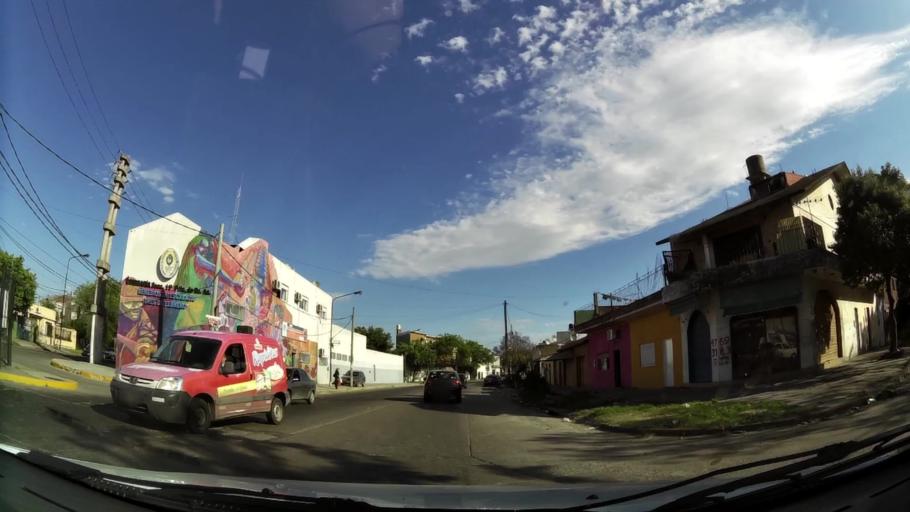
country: AR
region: Buenos Aires
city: Hurlingham
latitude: -34.5654
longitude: -58.6229
